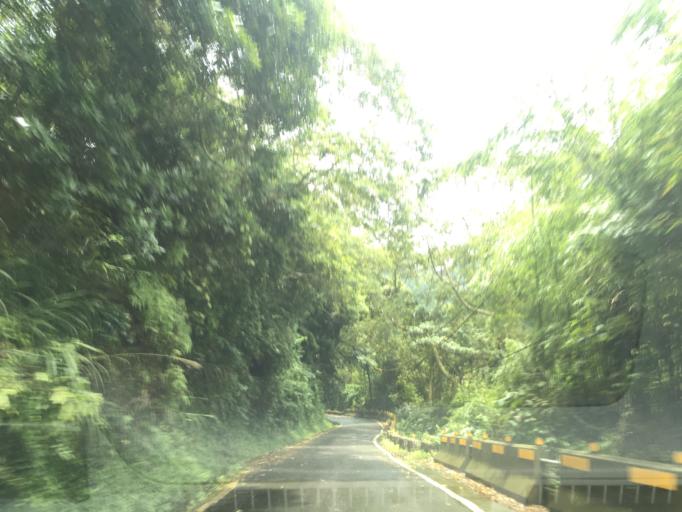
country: TW
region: Taiwan
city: Lugu
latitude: 23.5505
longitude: 120.6799
